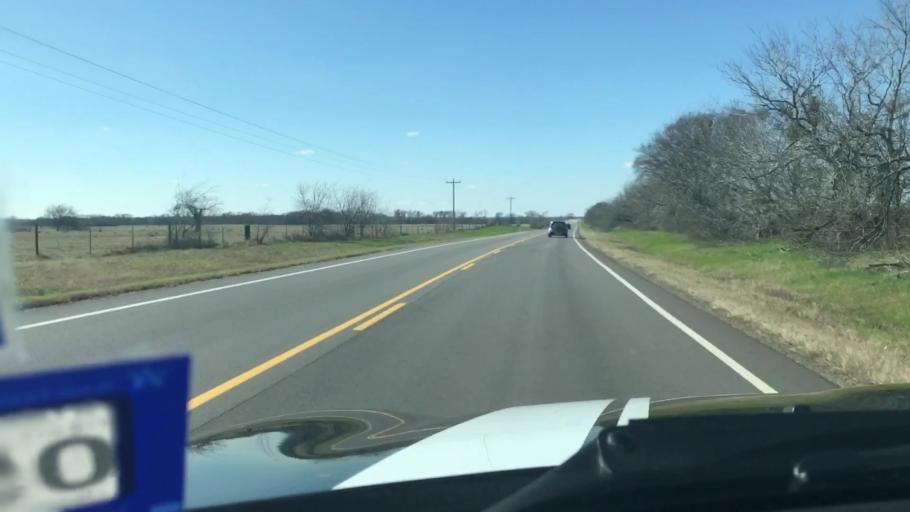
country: US
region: Texas
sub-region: Robertson County
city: Hearne
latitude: 30.8828
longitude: -96.6302
